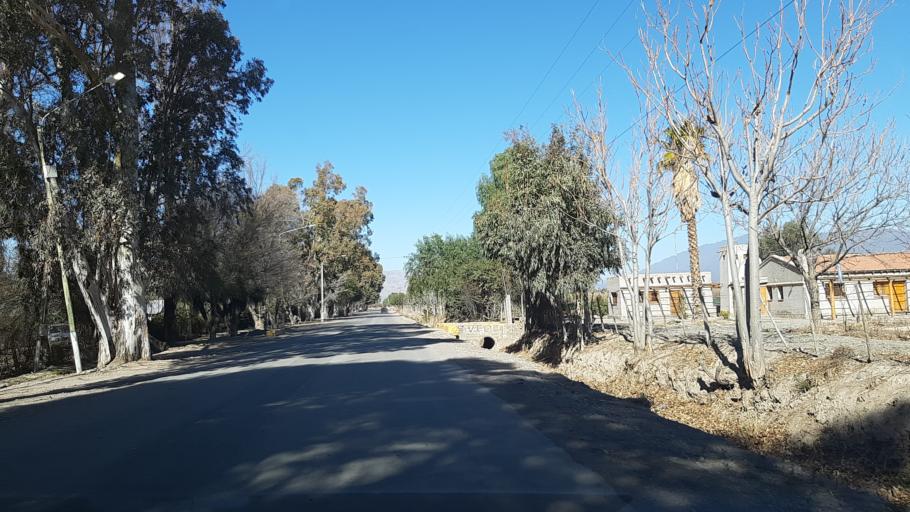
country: AR
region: San Juan
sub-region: Departamento de Zonda
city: Zonda
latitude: -31.4641
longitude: -68.7231
